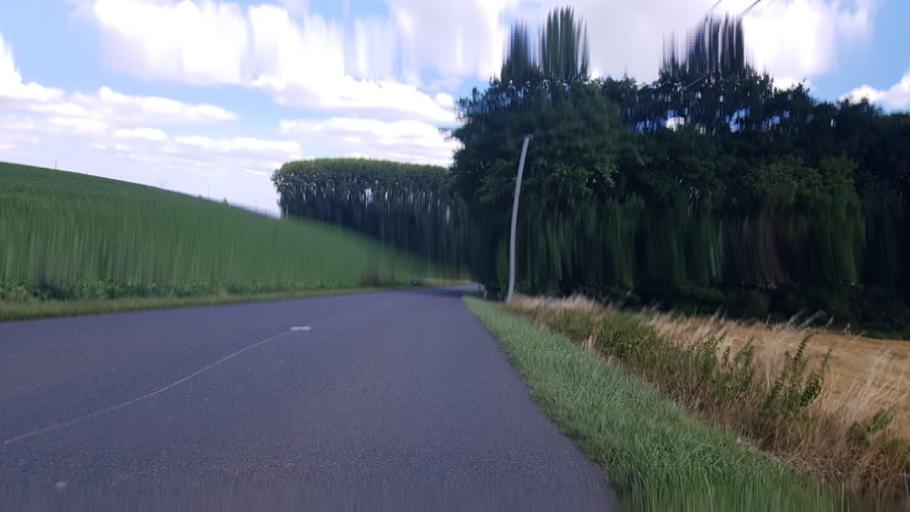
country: FR
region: Ile-de-France
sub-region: Departement de Seine-et-Marne
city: Moussy-le-Neuf
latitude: 49.0706
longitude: 2.6232
